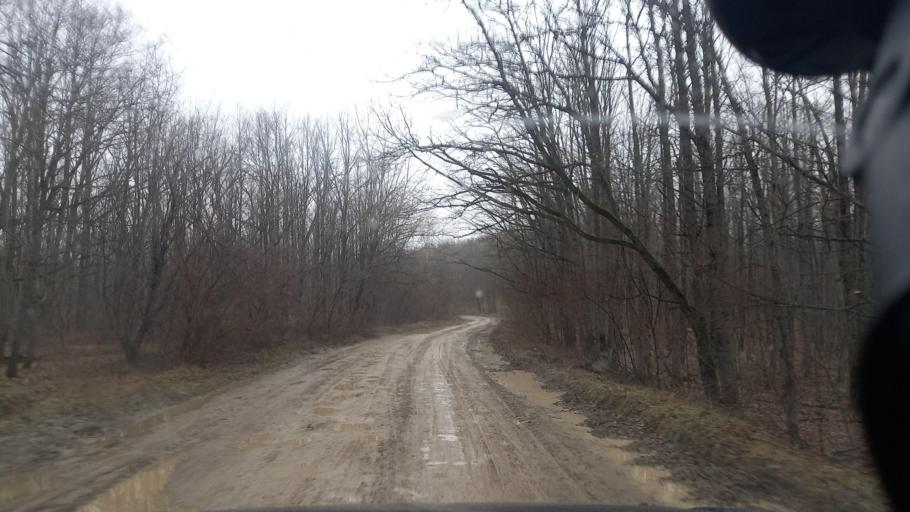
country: RU
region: Krasnodarskiy
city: Saratovskaya
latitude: 44.6482
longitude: 39.2463
